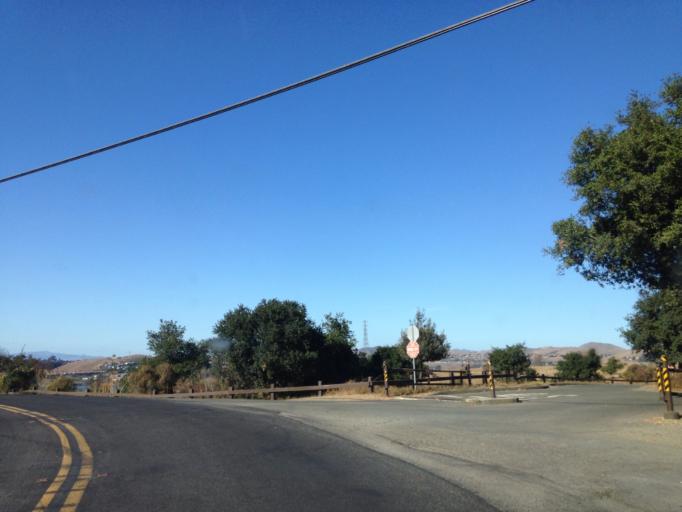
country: US
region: California
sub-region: Contra Costa County
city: Crockett
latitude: 38.0490
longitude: -122.1973
